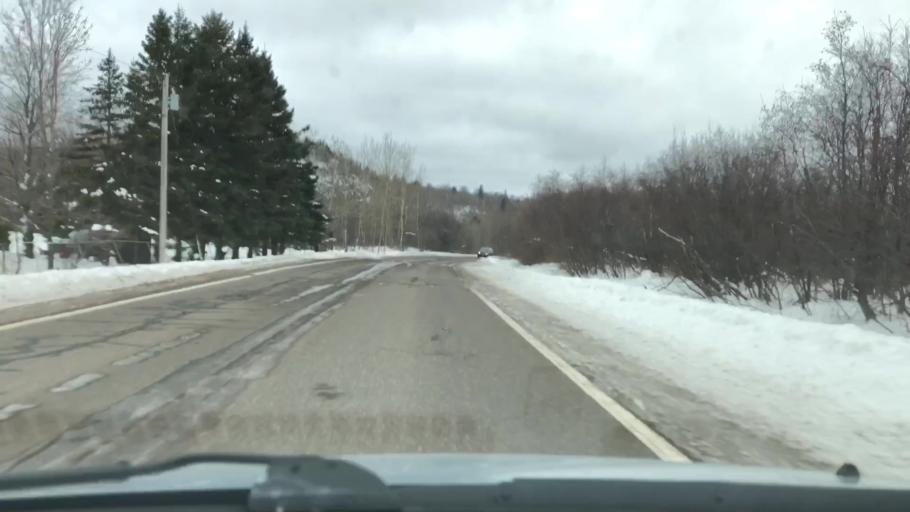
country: US
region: Minnesota
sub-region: Saint Louis County
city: Proctor
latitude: 46.7115
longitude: -92.2611
